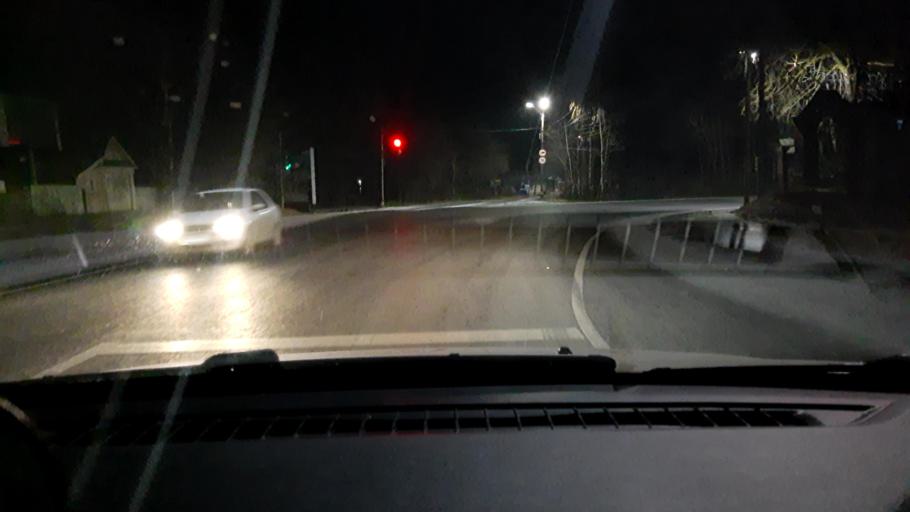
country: RU
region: Nizjnij Novgorod
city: Novaya Balakhna
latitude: 56.5173
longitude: 43.5813
